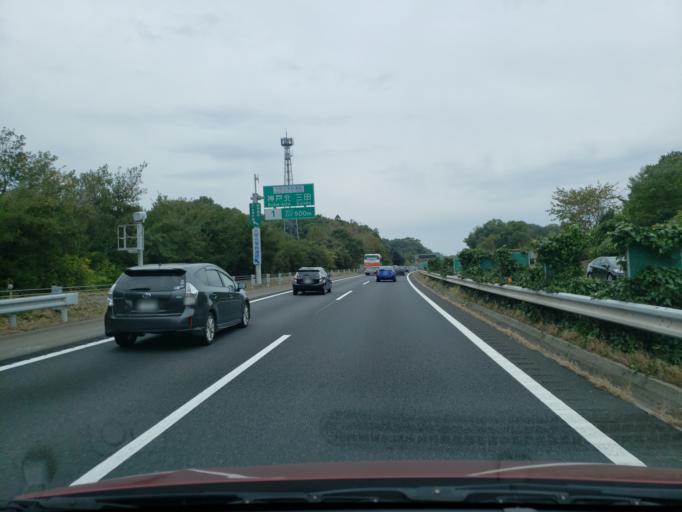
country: JP
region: Hyogo
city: Sandacho
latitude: 34.8369
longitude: 135.1912
